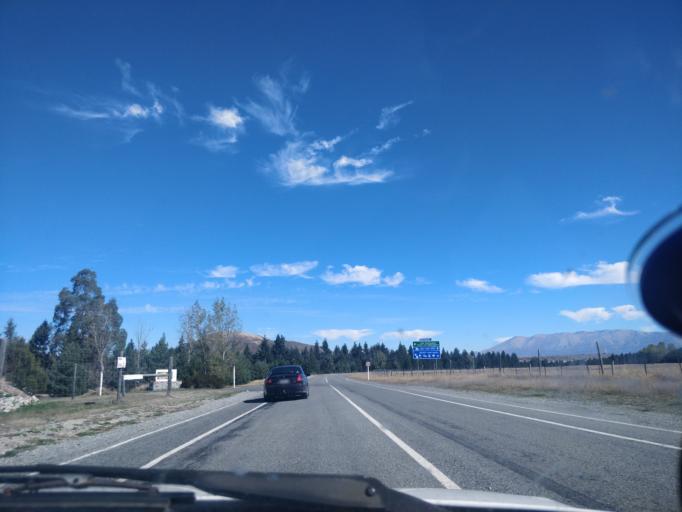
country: NZ
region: Otago
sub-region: Queenstown-Lakes District
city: Wanaka
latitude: -44.2707
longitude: 170.0625
